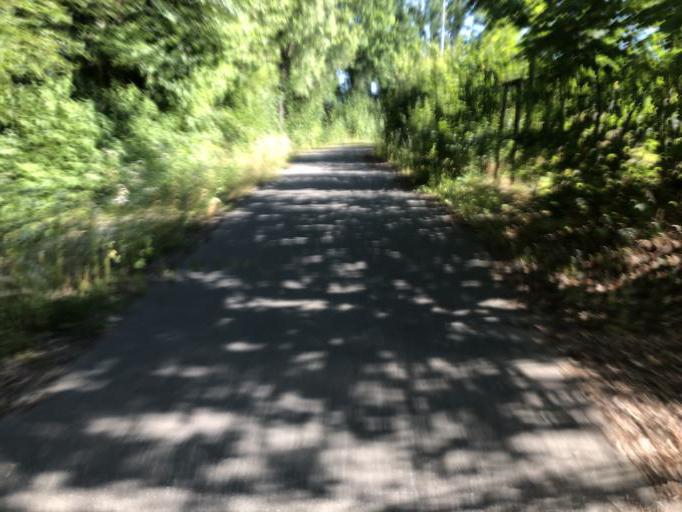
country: DE
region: Bavaria
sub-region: Regierungsbezirk Mittelfranken
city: Erlangen
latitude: 49.5614
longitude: 10.9762
